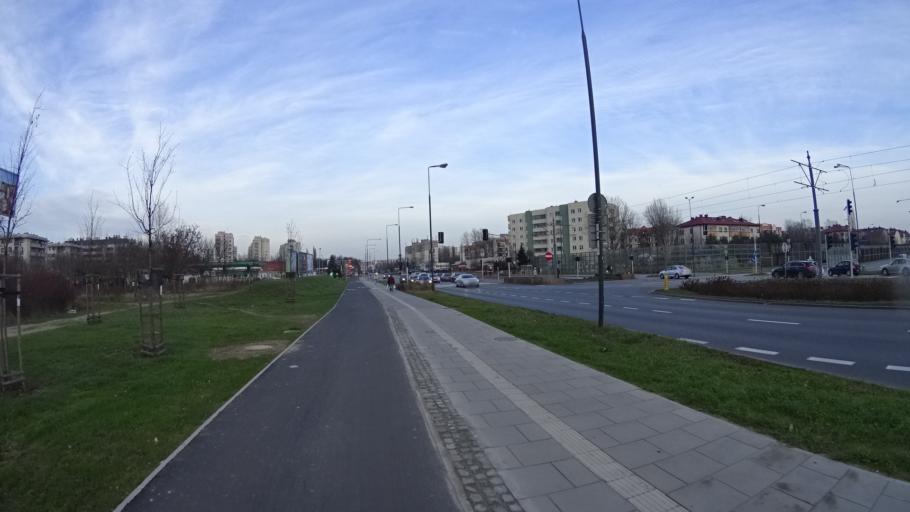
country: PL
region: Masovian Voivodeship
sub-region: Warszawa
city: Bielany
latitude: 52.2683
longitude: 20.9320
